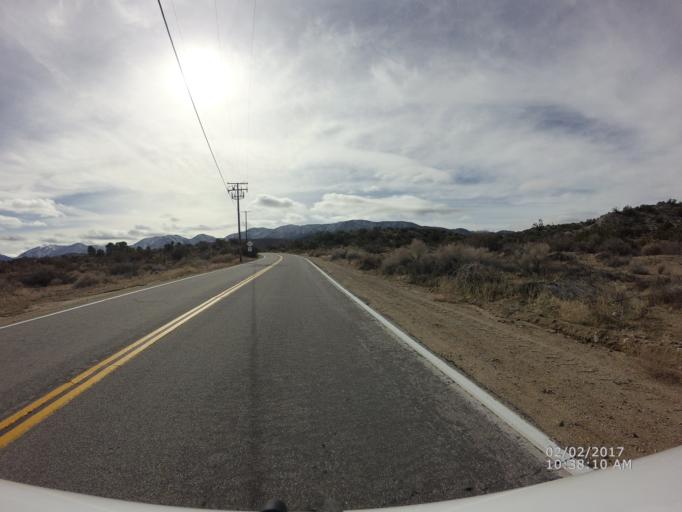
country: US
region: California
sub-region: Los Angeles County
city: Littlerock
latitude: 34.4791
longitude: -117.9361
